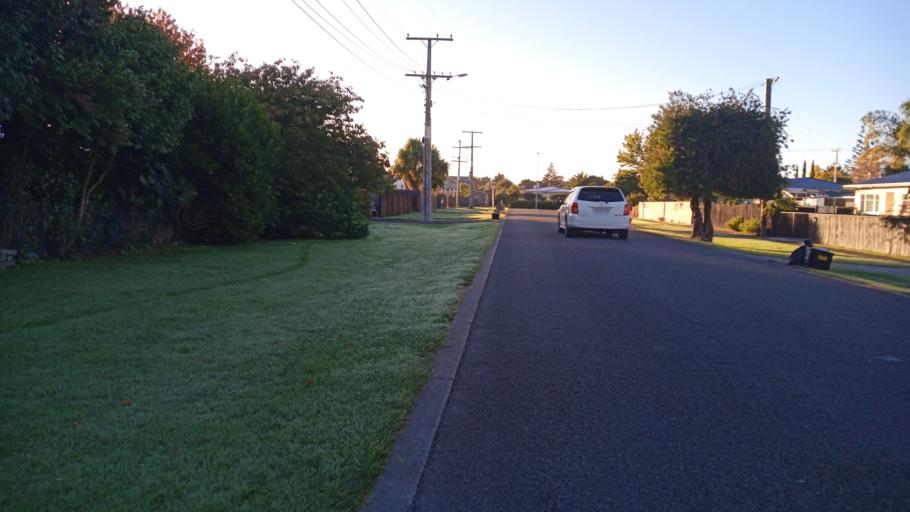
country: NZ
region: Gisborne
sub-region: Gisborne District
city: Gisborne
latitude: -38.6536
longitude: 177.9959
